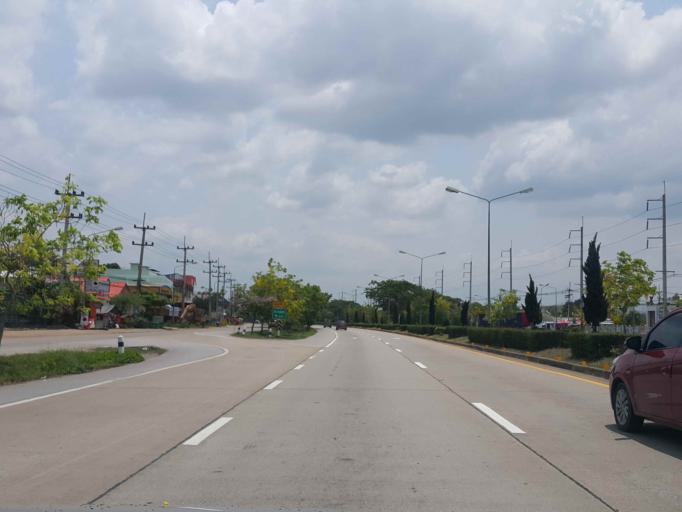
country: TH
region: Lampang
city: Lampang
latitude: 18.2781
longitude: 99.4541
